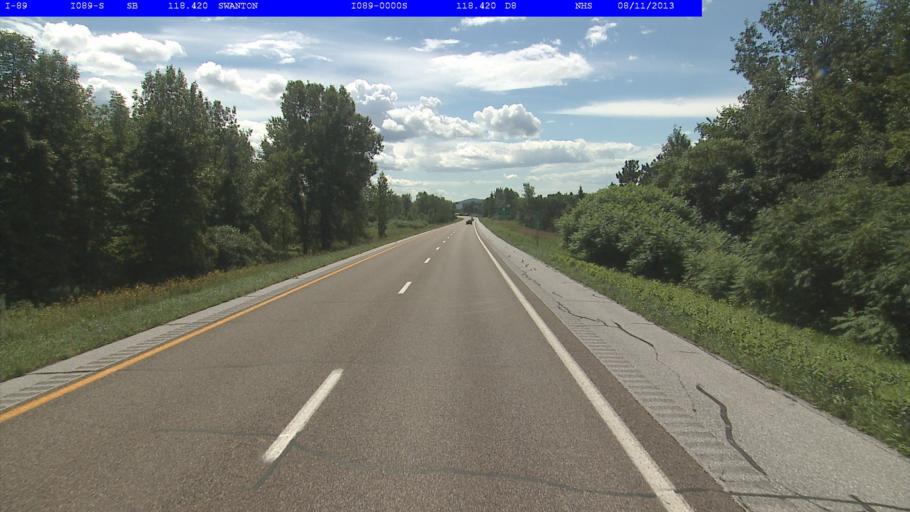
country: US
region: Vermont
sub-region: Franklin County
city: Saint Albans
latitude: 44.8543
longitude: -73.0827
